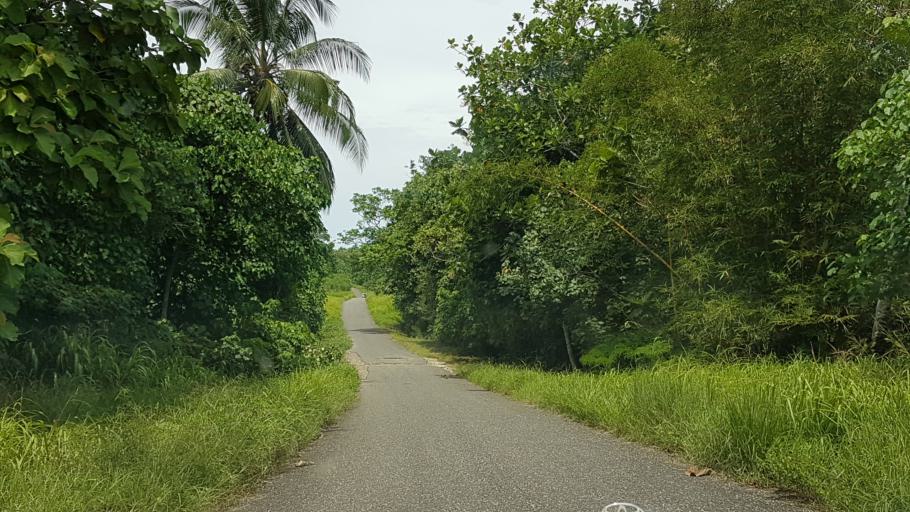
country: PG
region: Madang
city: Madang
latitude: -4.5808
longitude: 145.5203
